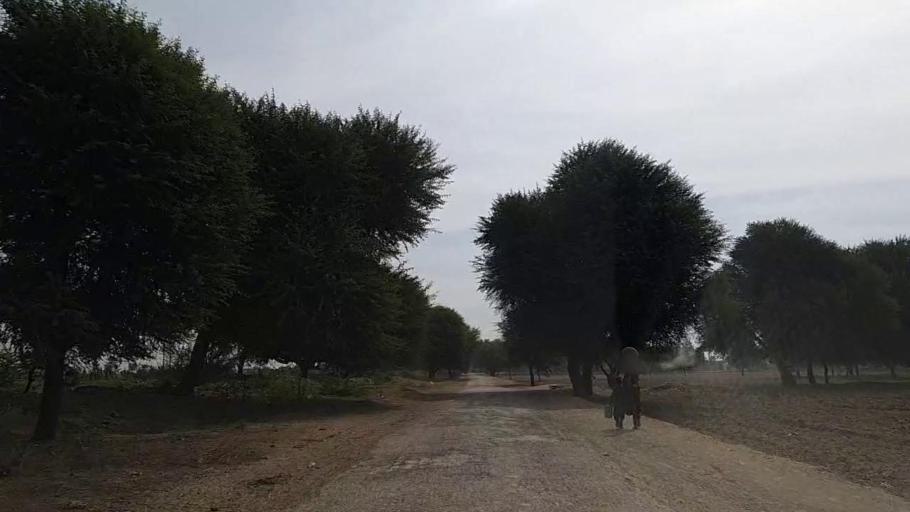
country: PK
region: Sindh
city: Samaro
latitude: 25.2855
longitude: 69.4203
